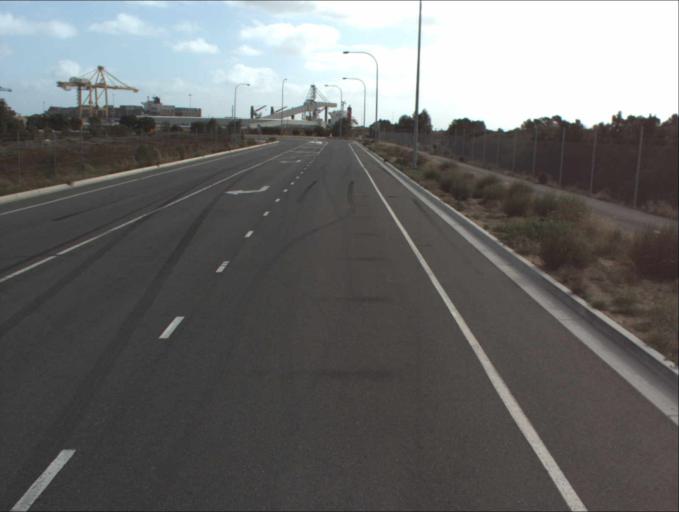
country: AU
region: South Australia
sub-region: Port Adelaide Enfield
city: Birkenhead
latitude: -34.7677
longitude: 138.5035
